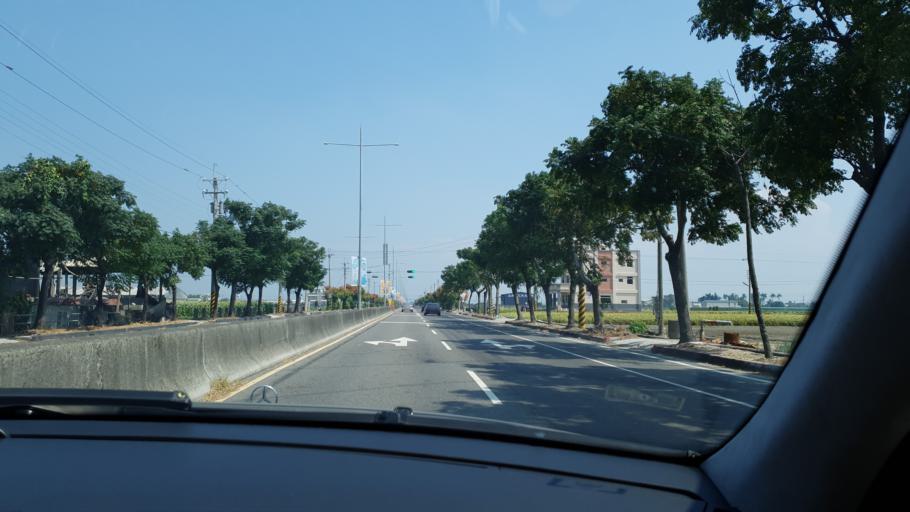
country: TW
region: Taiwan
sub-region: Yunlin
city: Douliu
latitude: 23.7356
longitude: 120.4521
